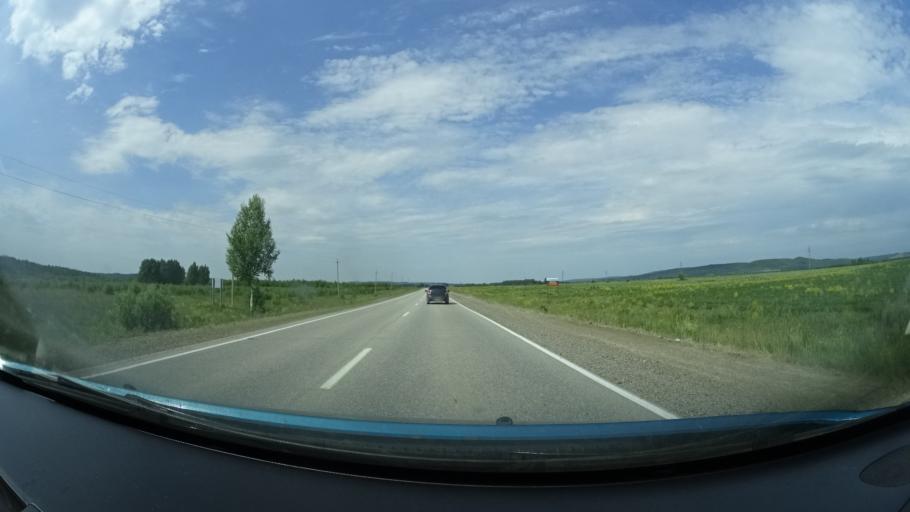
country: RU
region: Perm
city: Barda
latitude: 57.0455
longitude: 55.5456
